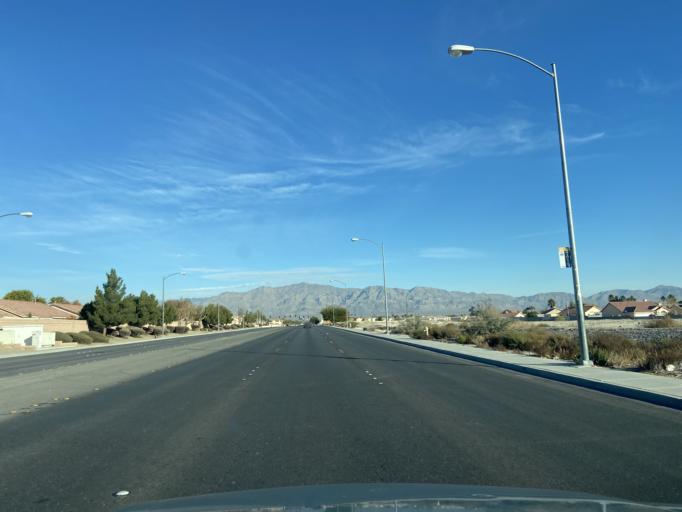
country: US
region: Nevada
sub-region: Clark County
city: North Las Vegas
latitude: 36.2436
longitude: -115.1801
